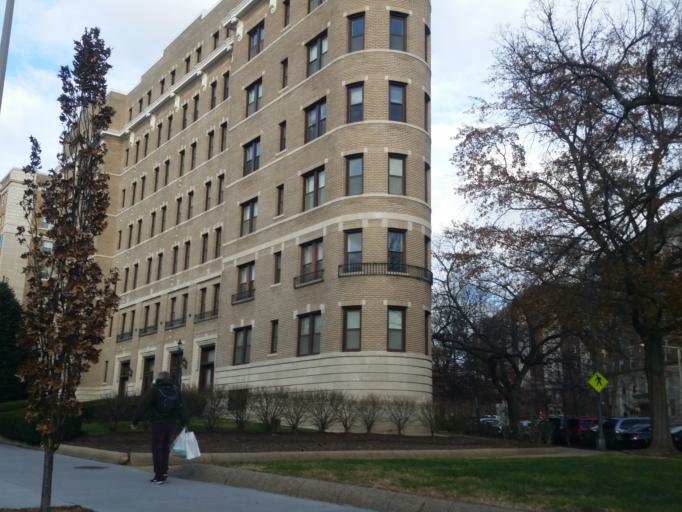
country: US
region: Washington, D.C.
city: Washington, D.C.
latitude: 38.9175
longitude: -77.0364
